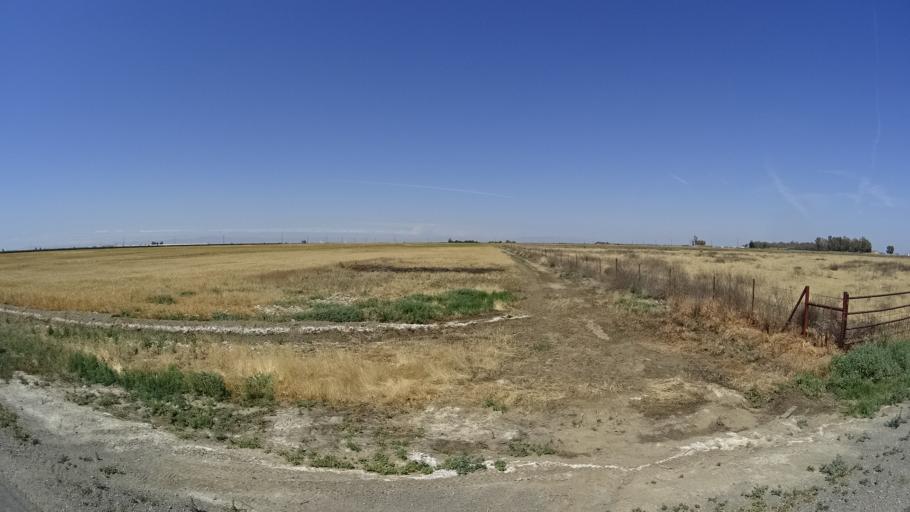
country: US
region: California
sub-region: Kings County
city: Stratford
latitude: 36.2367
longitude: -119.7985
